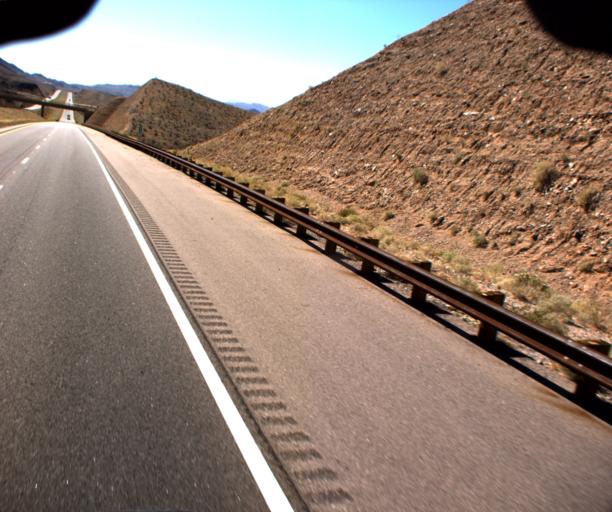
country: US
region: Nevada
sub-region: Clark County
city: Boulder City
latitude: 35.8918
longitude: -114.6239
